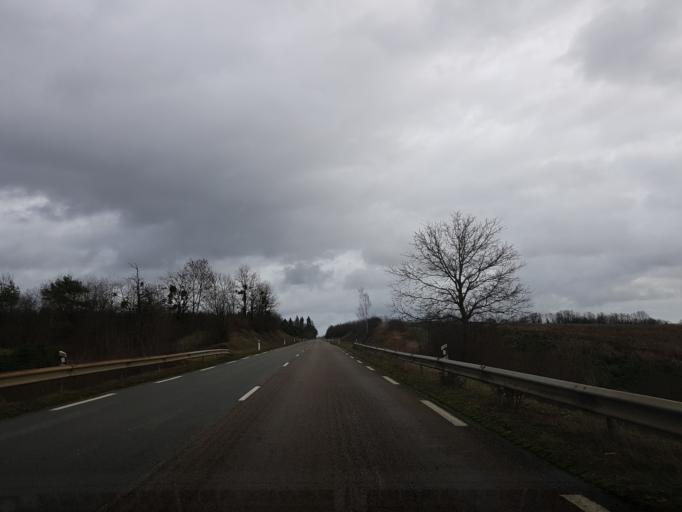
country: FR
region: Franche-Comte
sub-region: Departement de la Haute-Saone
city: Scey-sur-Saone-et-Saint-Albin
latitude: 47.6999
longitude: 5.9503
